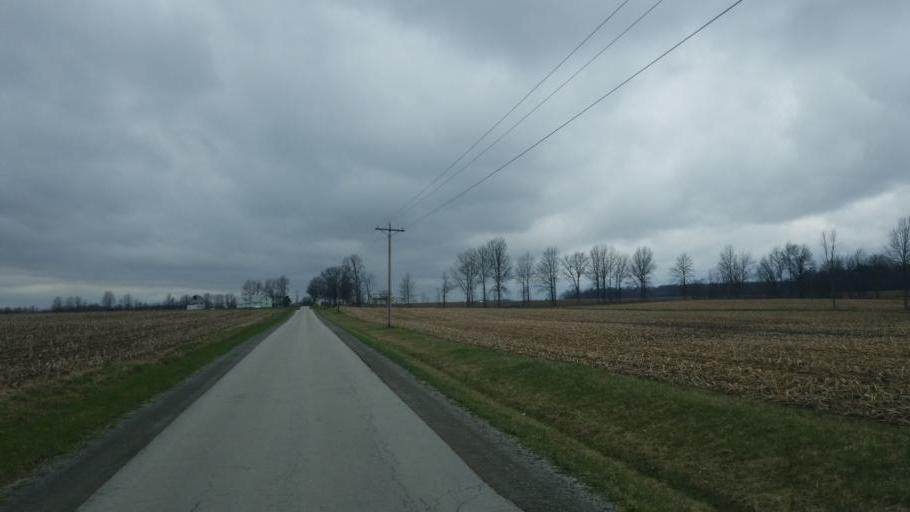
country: US
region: Ohio
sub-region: Hardin County
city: Forest
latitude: 40.7377
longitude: -83.4316
